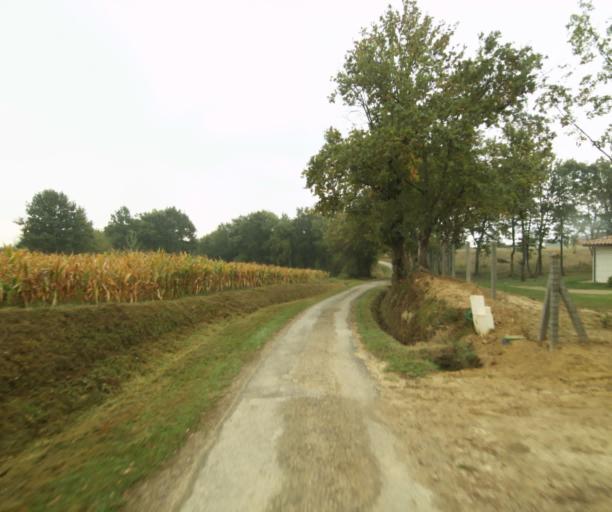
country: FR
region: Midi-Pyrenees
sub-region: Departement du Gers
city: Cazaubon
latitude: 43.9282
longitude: -0.1109
